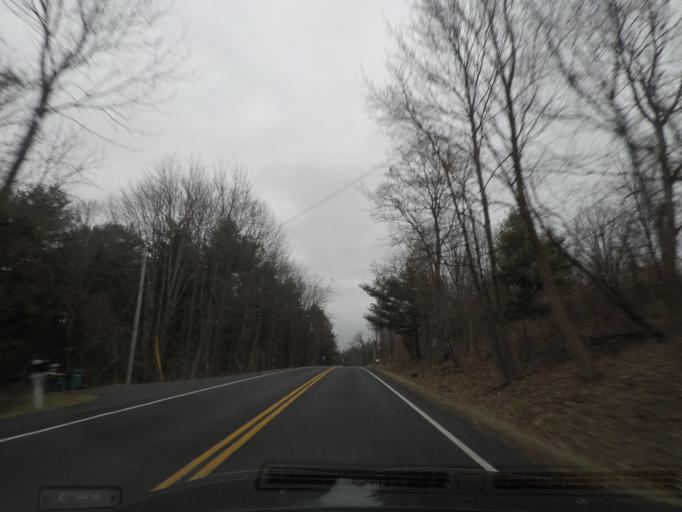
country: US
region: New York
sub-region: Rensselaer County
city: East Greenbush
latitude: 42.5991
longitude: -73.6467
